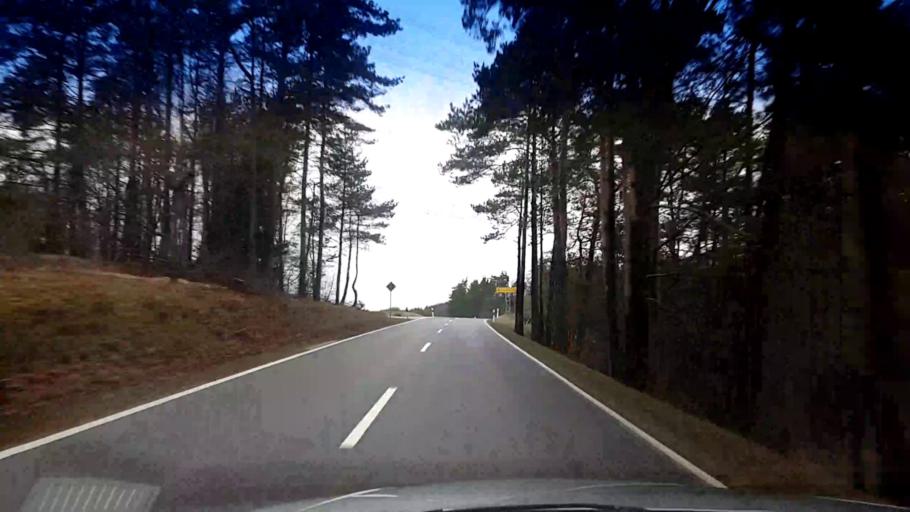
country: DE
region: Bavaria
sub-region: Upper Franconia
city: Wattendorf
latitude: 50.0211
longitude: 11.1265
